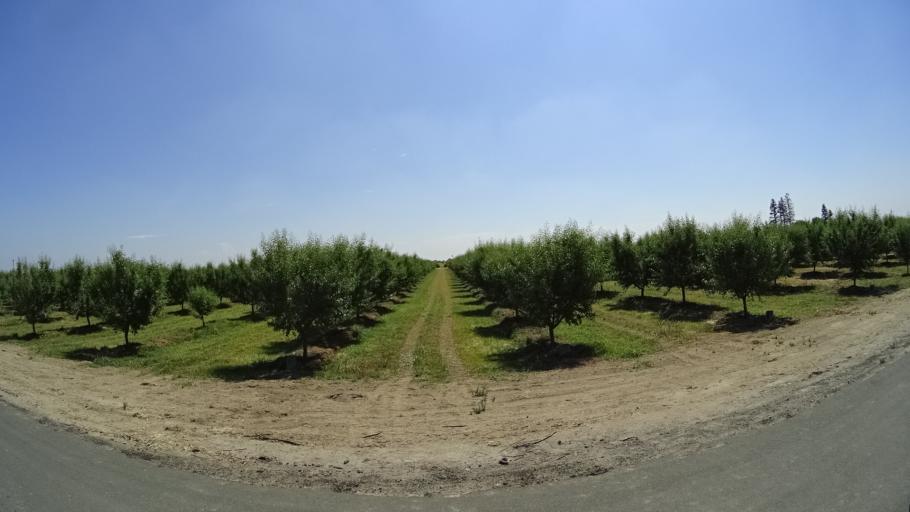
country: US
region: California
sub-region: Fresno County
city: Kingsburg
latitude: 36.4619
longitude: -119.5734
